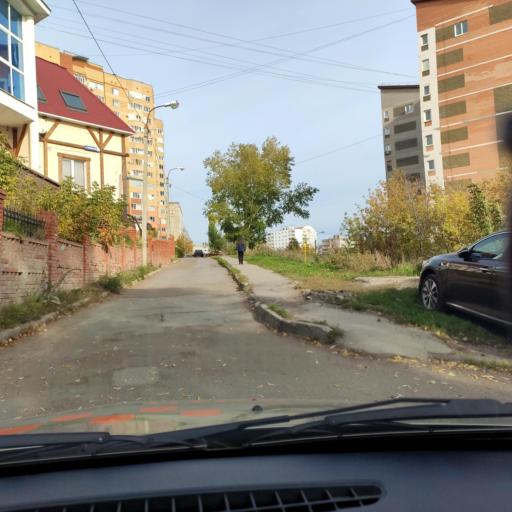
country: RU
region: Bashkortostan
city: Ufa
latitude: 54.7012
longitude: 55.9884
